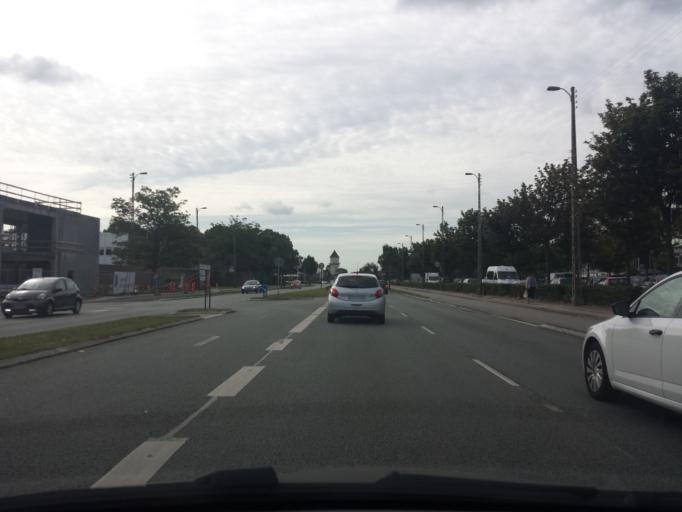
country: DK
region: Capital Region
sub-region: Rodovre Kommune
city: Rodovre
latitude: 55.6831
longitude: 12.4522
